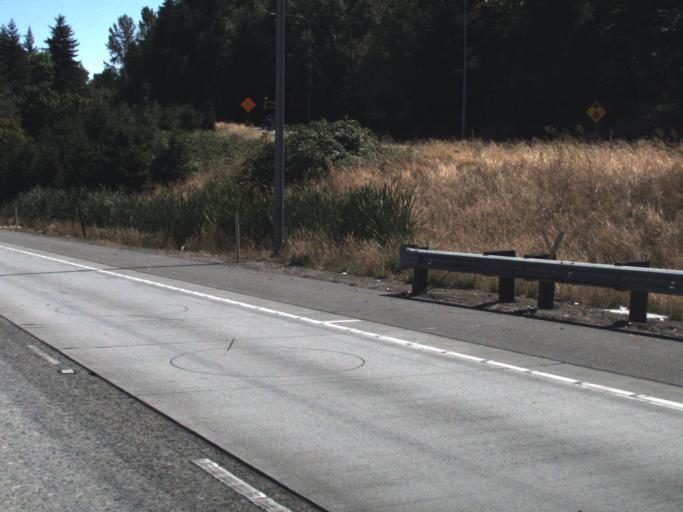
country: US
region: Washington
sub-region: King County
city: Tukwila
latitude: 47.4640
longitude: -122.2716
